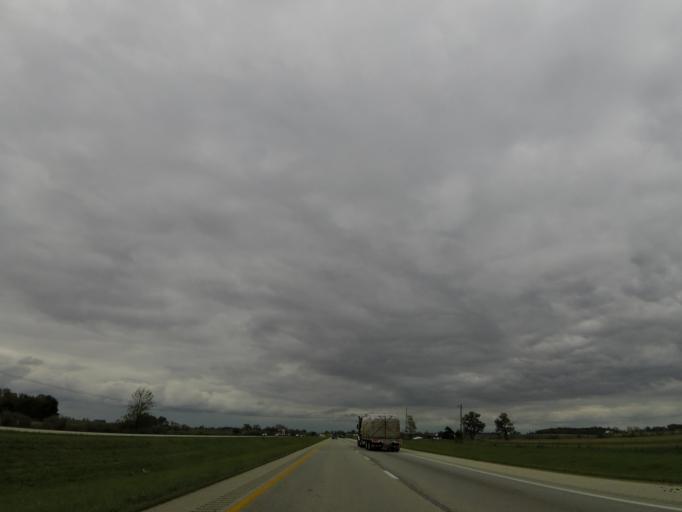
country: US
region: Ohio
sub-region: Greene County
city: Jamestown
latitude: 39.5477
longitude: -83.7466
